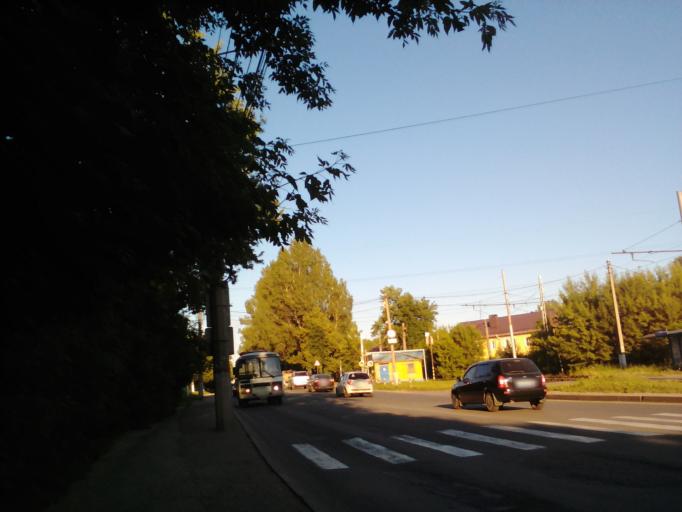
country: RU
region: Kursk
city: Voroshnevo
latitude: 51.6678
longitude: 36.0976
